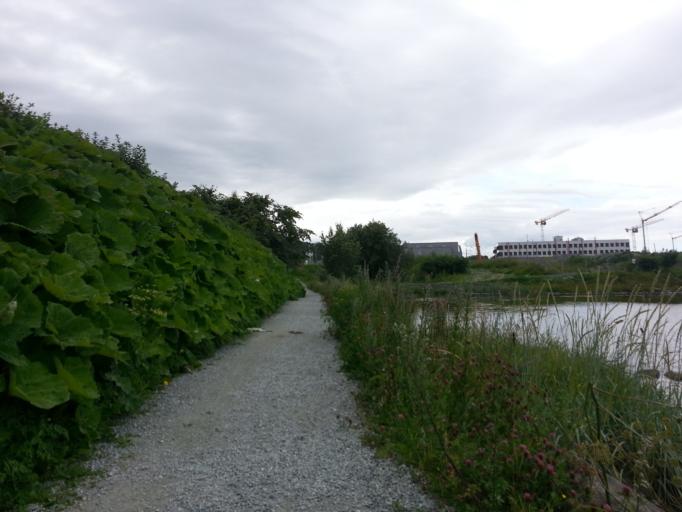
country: NO
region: Sor-Trondelag
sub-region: Trondheim
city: Trondheim
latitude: 63.4329
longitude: 10.5127
